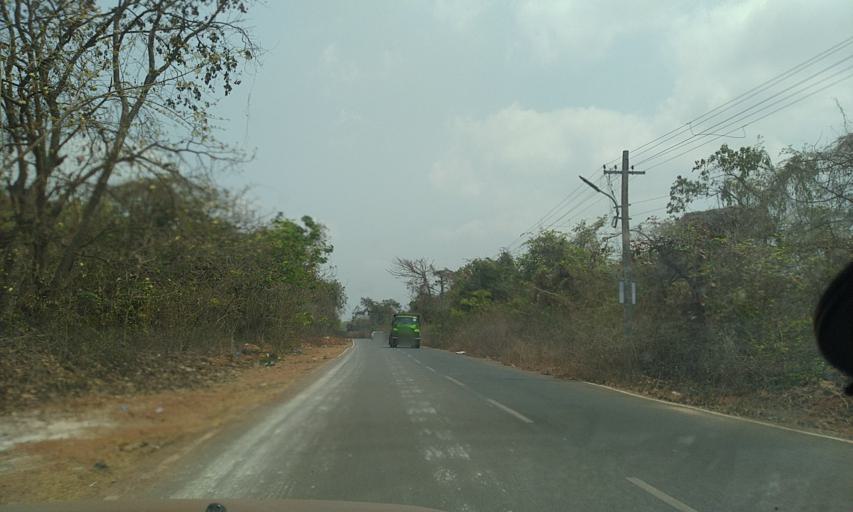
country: IN
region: Goa
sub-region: North Goa
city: Goa Velha
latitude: 15.4871
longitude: 73.9102
